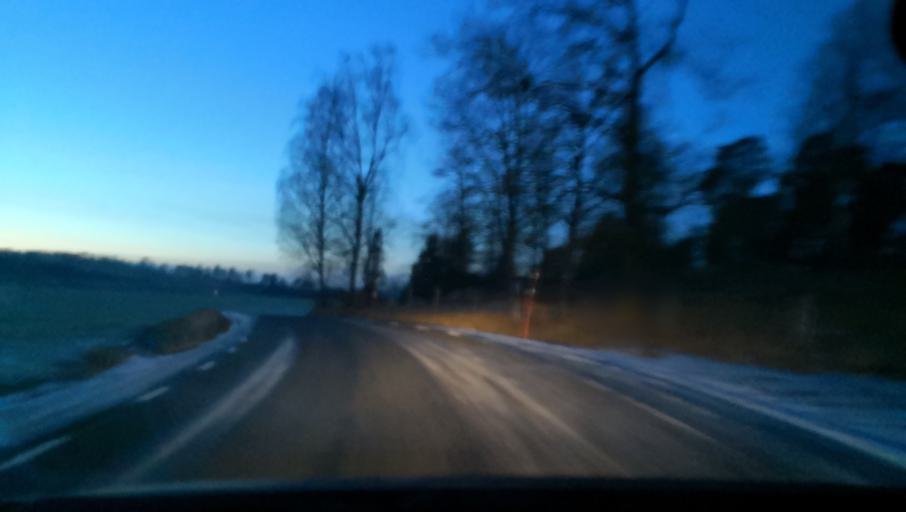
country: SE
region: Soedermanland
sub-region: Katrineholms Kommun
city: Katrineholm
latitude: 59.0713
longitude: 16.3535
